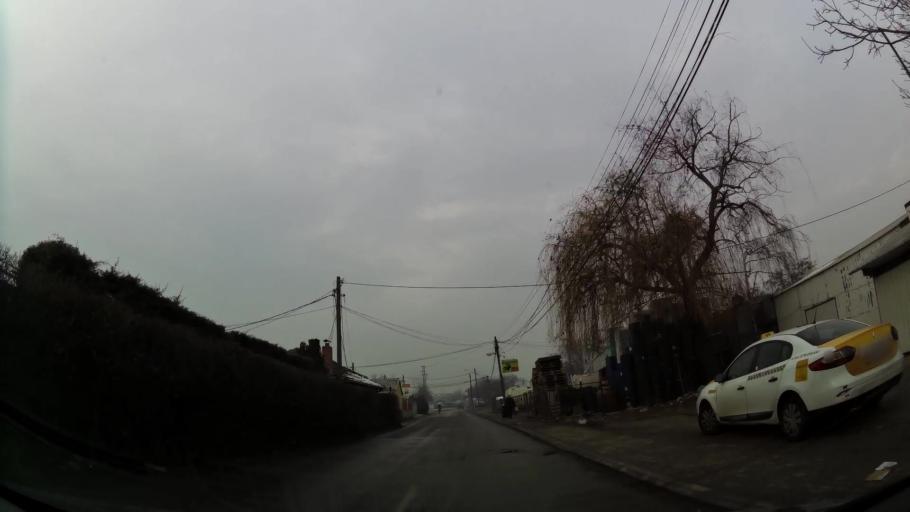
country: MK
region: Kisela Voda
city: Kisela Voda
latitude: 41.9963
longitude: 21.4913
